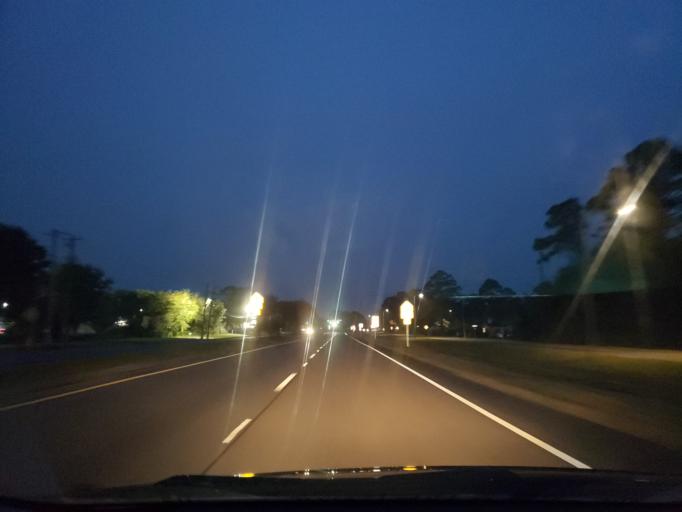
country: US
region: Georgia
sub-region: Chatham County
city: Whitemarsh Island
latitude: 32.0436
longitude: -81.0076
